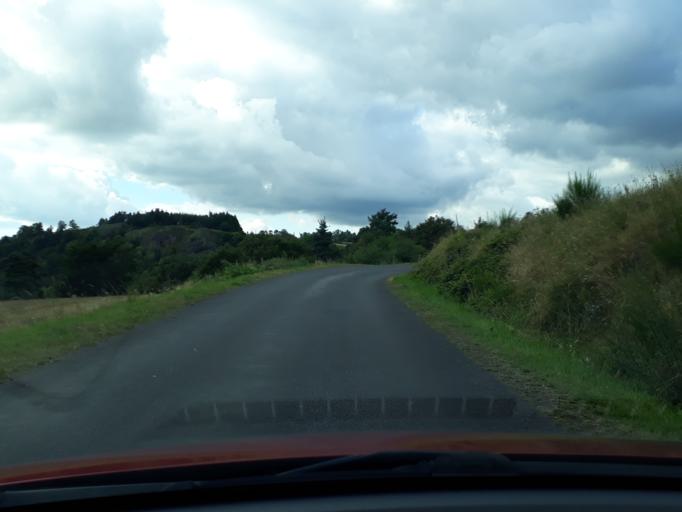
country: FR
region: Auvergne
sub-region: Departement de la Haute-Loire
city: Le Monastier-sur-Gazeille
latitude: 44.8323
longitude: 3.9446
